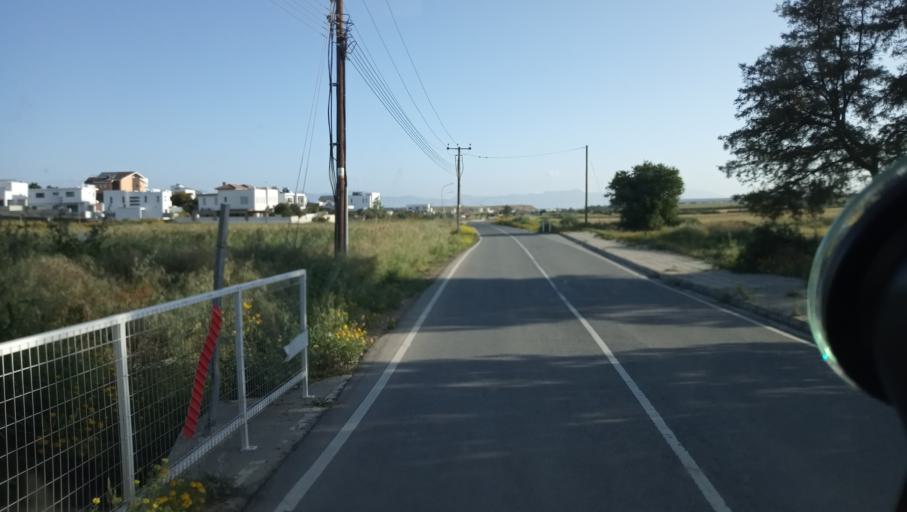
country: CY
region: Lefkosia
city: Geri
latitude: 35.0695
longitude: 33.3982
